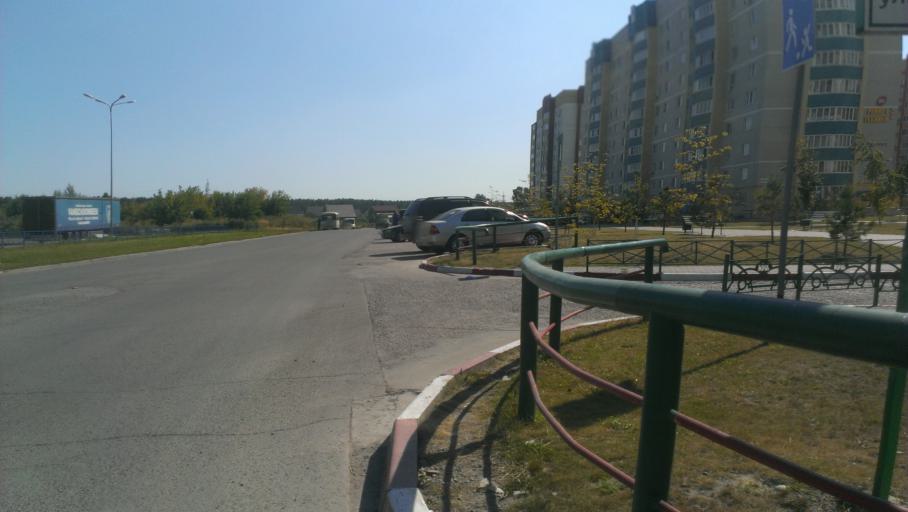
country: RU
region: Altai Krai
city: Novosilikatnyy
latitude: 53.3267
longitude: 83.6832
